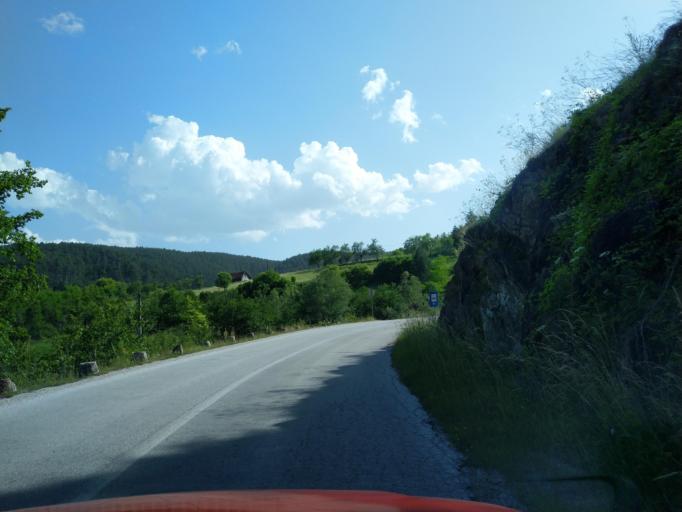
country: RS
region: Central Serbia
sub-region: Zlatiborski Okrug
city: Bajina Basta
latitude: 43.8493
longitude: 19.6230
